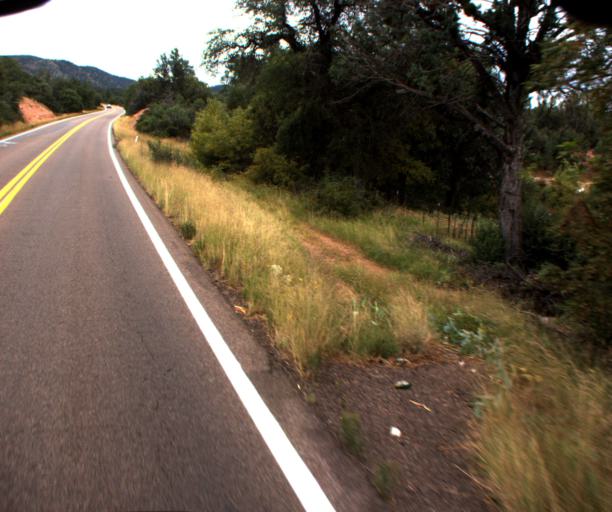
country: US
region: Arizona
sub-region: Gila County
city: Star Valley
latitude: 34.2623
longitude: -111.2126
